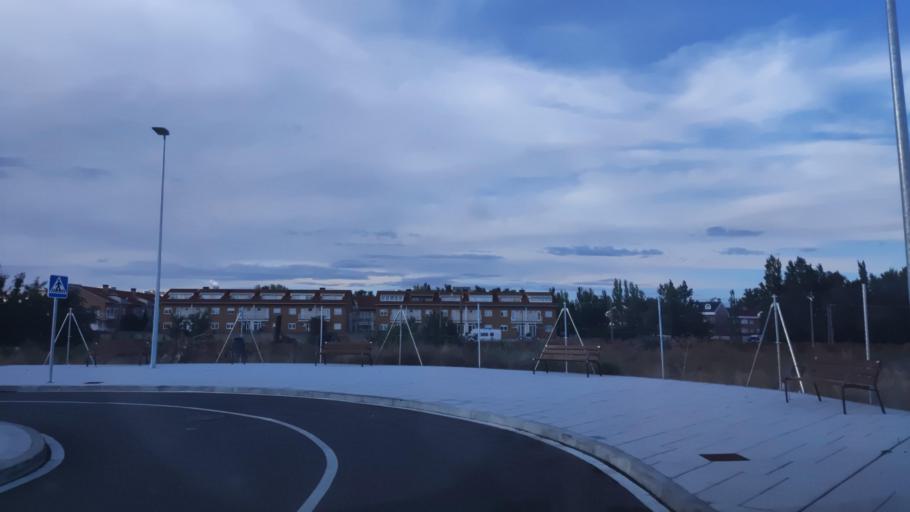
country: ES
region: Castille and Leon
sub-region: Provincia de Salamanca
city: Carbajosa de la Sagrada
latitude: 40.9533
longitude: -5.6505
